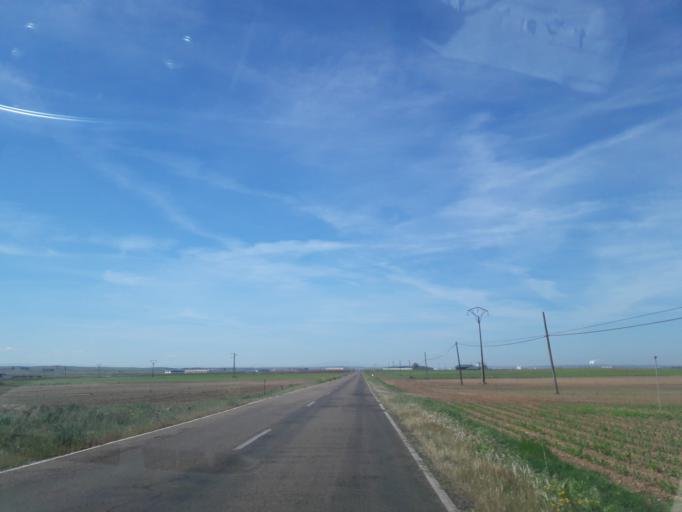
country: ES
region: Castille and Leon
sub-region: Provincia de Salamanca
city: Villoruela
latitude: 41.0000
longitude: -5.4001
